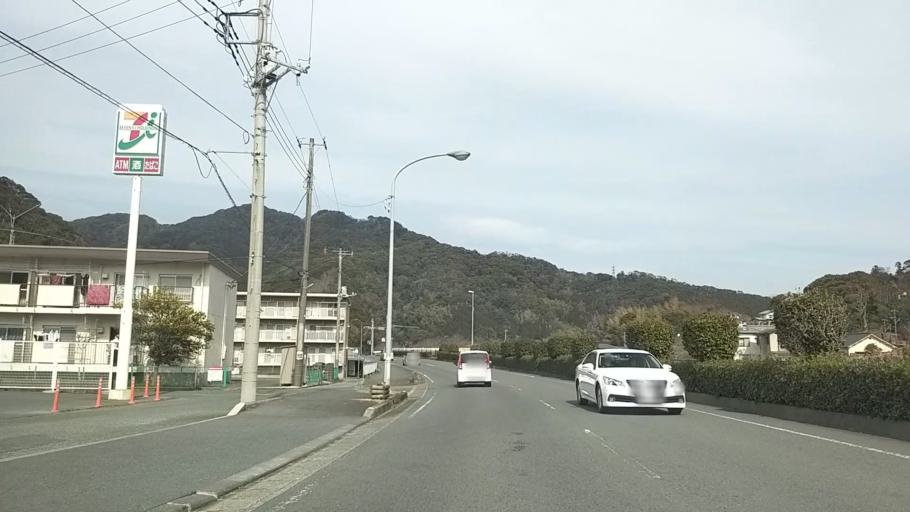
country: JP
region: Shizuoka
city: Shimoda
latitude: 34.7014
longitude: 138.9406
